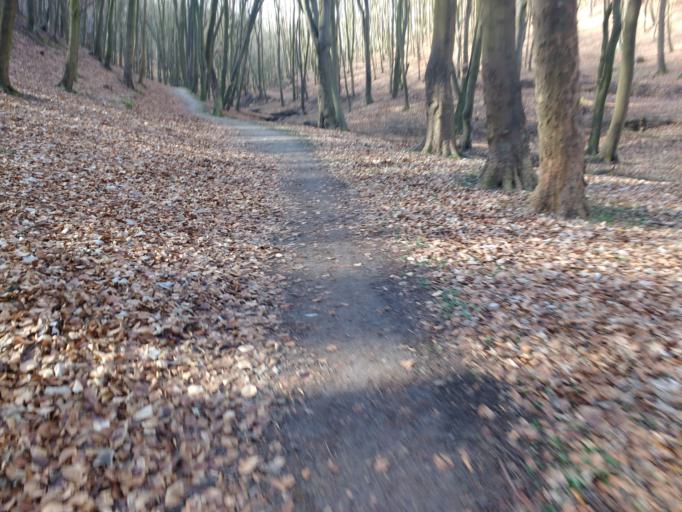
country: PL
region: Pomeranian Voivodeship
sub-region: Gdynia
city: Wielki Kack
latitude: 54.4816
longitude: 18.5158
